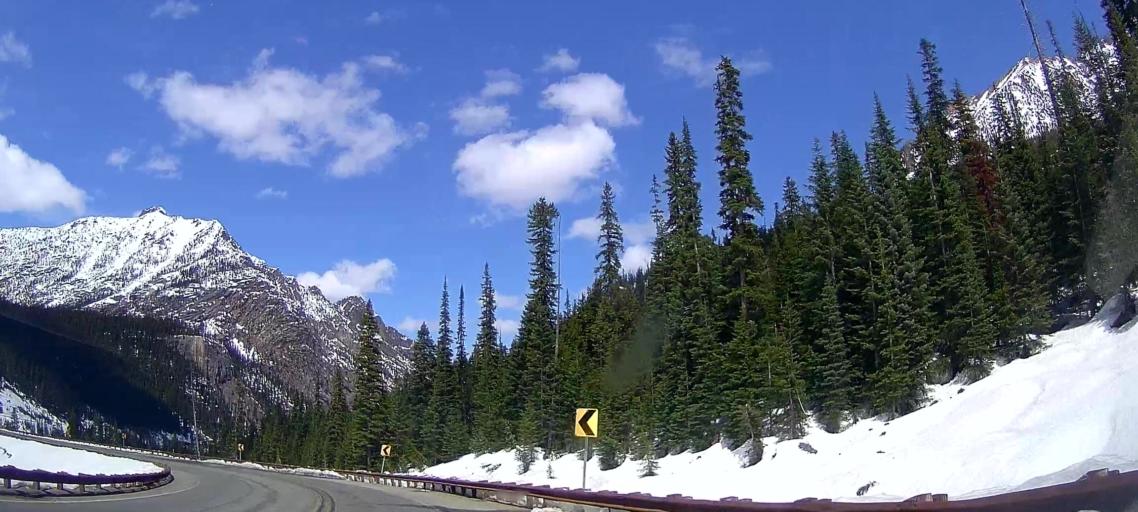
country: US
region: Washington
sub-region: Chelan County
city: Granite Falls
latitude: 48.5165
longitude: -120.6427
